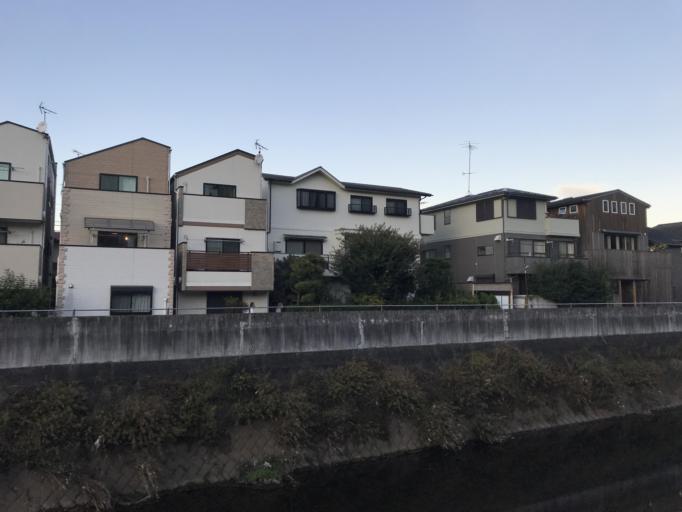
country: JP
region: Kanagawa
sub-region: Kawasaki-shi
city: Kawasaki
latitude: 35.5607
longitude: 139.6454
